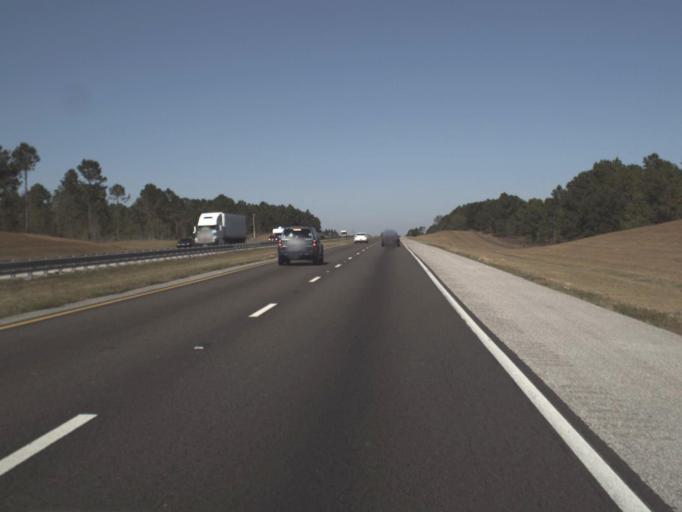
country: US
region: Florida
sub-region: Lake County
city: Minneola
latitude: 28.5953
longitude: -81.7158
